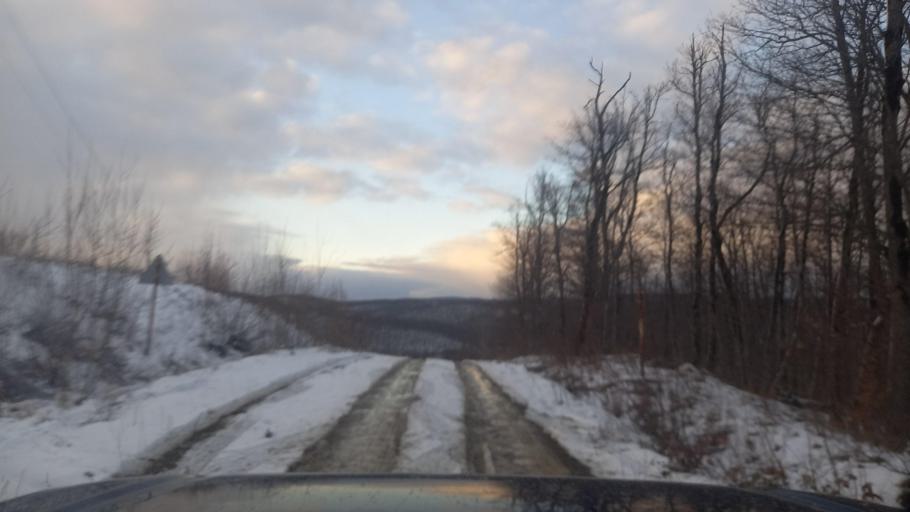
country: RU
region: Krasnodarskiy
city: Smolenskaya
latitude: 44.6773
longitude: 38.7948
